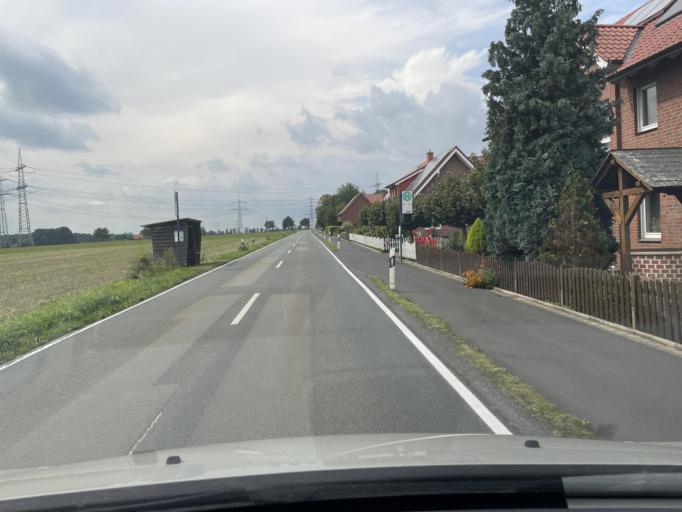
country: DE
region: North Rhine-Westphalia
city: Ahlen
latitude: 51.7532
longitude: 7.8421
